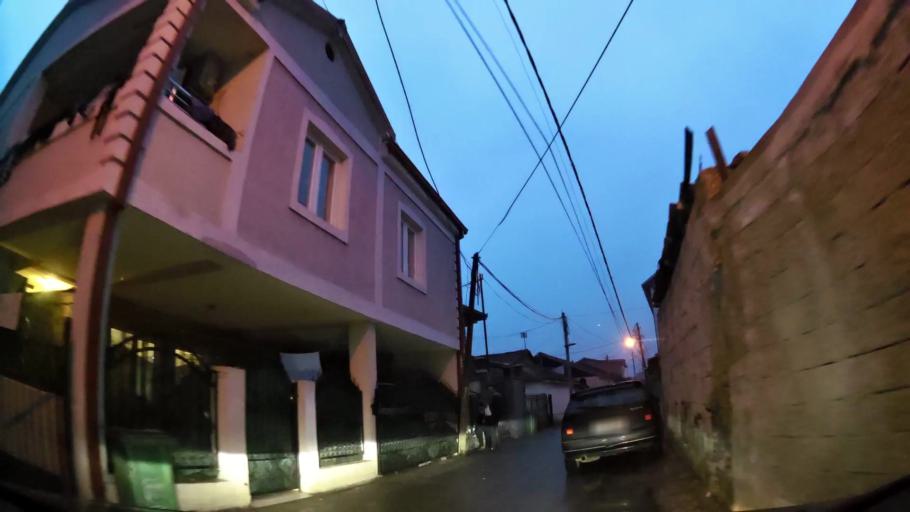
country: MK
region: Kisela Voda
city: Kisela Voda
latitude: 41.9647
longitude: 21.4866
